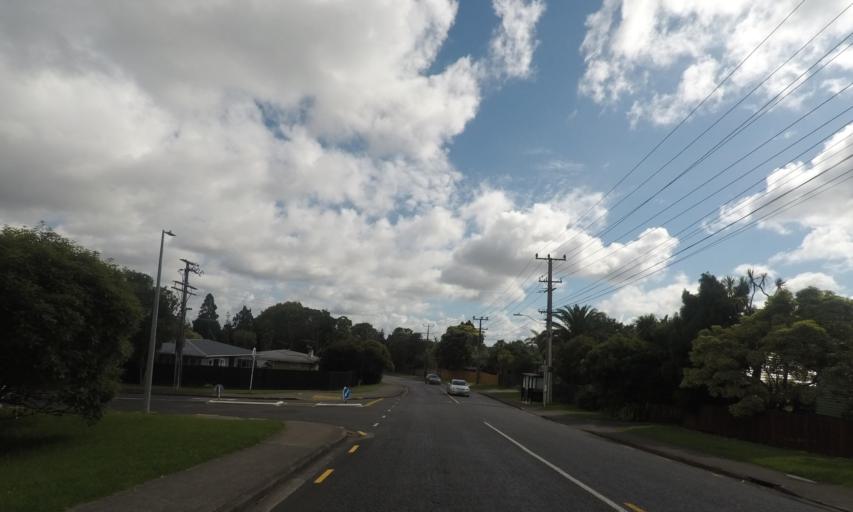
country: NZ
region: Auckland
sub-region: Auckland
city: Titirangi
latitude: -36.9327
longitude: 174.6553
